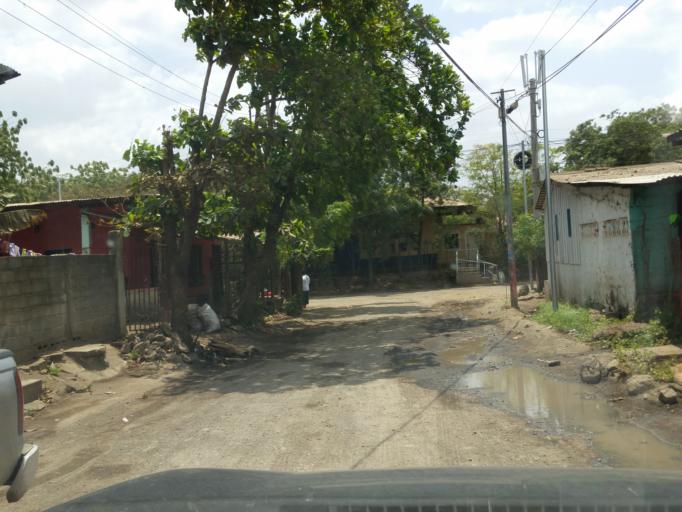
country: NI
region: Managua
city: Managua
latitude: 12.1171
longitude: -86.1660
